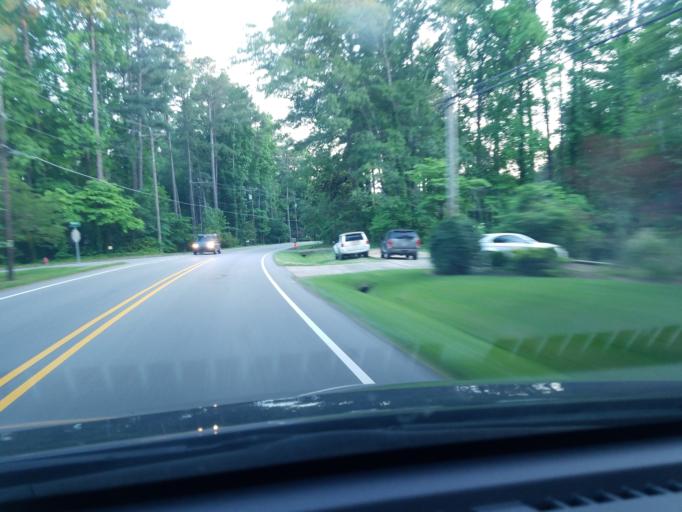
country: US
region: North Carolina
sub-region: Durham County
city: Durham
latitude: 35.9382
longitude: -78.9449
